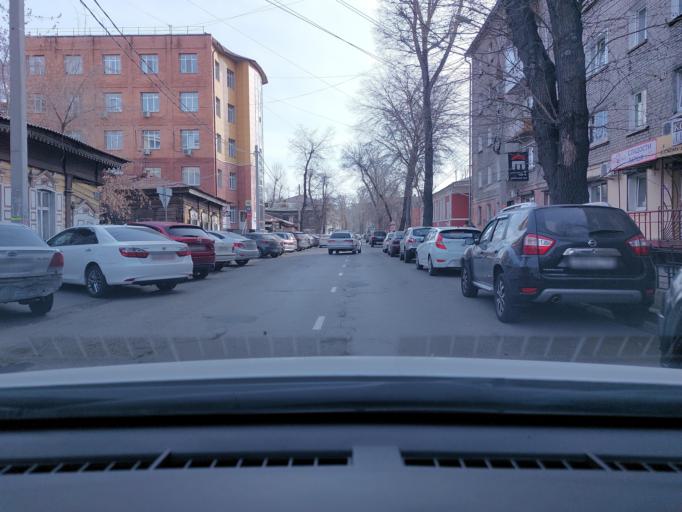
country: RU
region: Irkutsk
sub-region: Irkutskiy Rayon
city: Irkutsk
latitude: 52.2809
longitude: 104.2884
